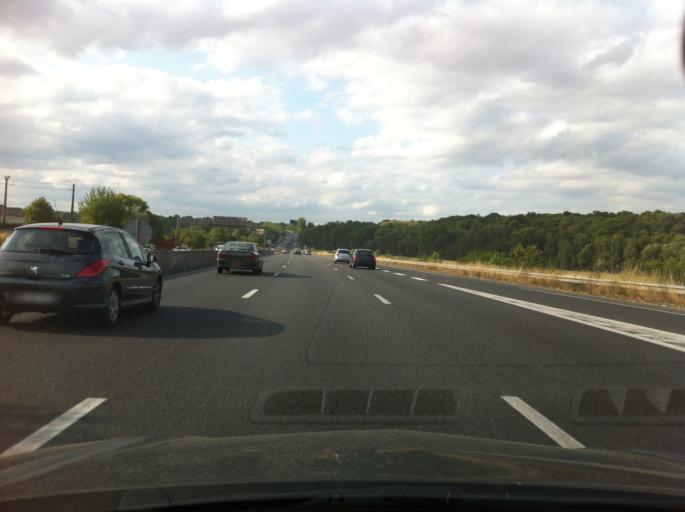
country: FR
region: Ile-de-France
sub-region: Departement de Seine-et-Marne
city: Brie-Comte-Robert
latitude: 48.6638
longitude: 2.6135
